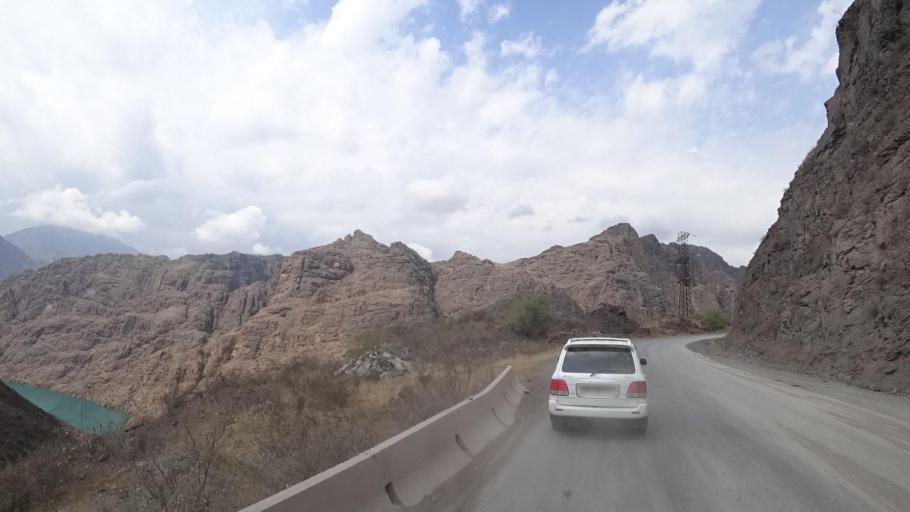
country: KG
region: Jalal-Abad
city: Tash-Kumyr
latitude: 41.5858
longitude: 72.5644
